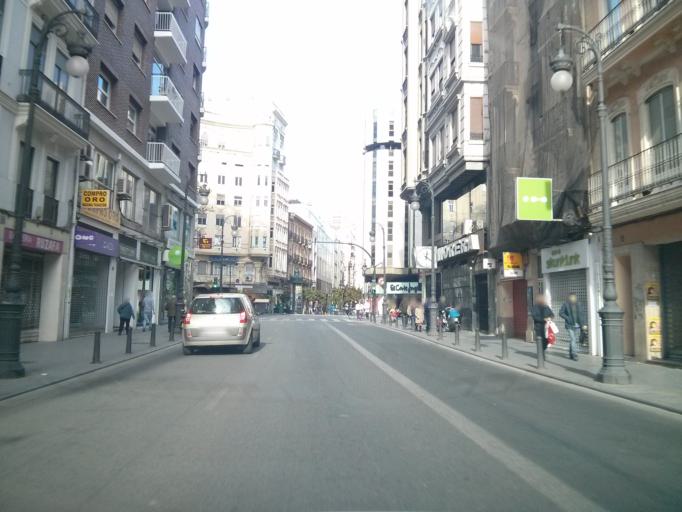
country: ES
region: Valencia
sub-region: Provincia de Valencia
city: Valencia
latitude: 39.4666
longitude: -0.3746
